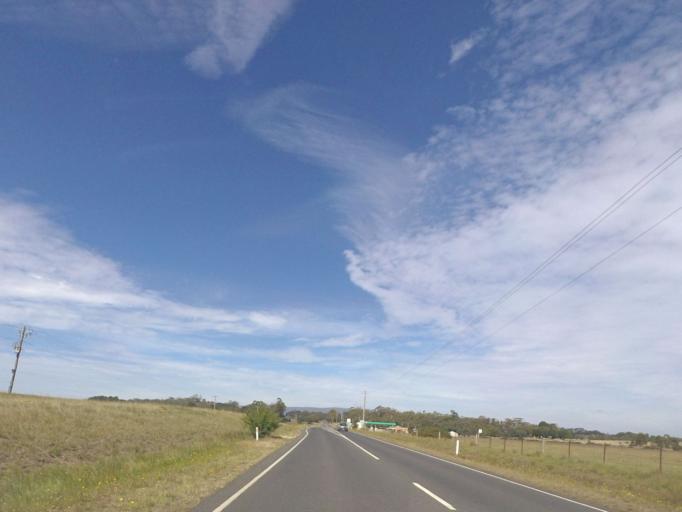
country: AU
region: Victoria
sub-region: Mount Alexander
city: Castlemaine
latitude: -37.2891
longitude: 144.5038
